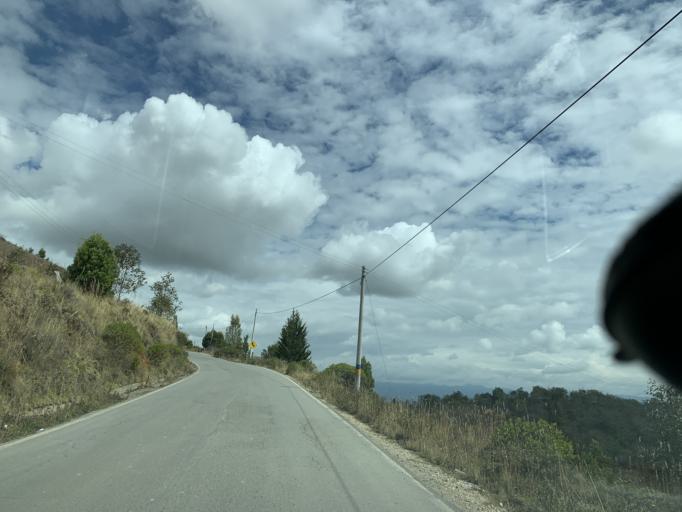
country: CO
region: Boyaca
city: Siachoque
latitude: 5.5746
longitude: -73.2679
